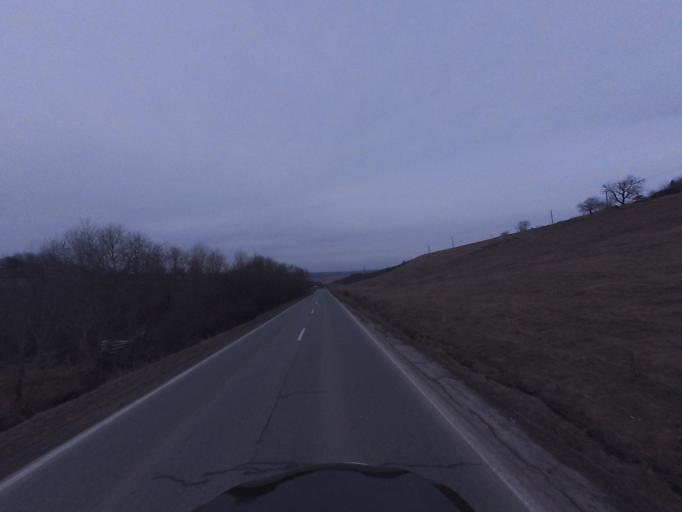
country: RO
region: Iasi
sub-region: Comuna Popricani
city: Popricani
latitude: 47.2913
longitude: 27.5113
